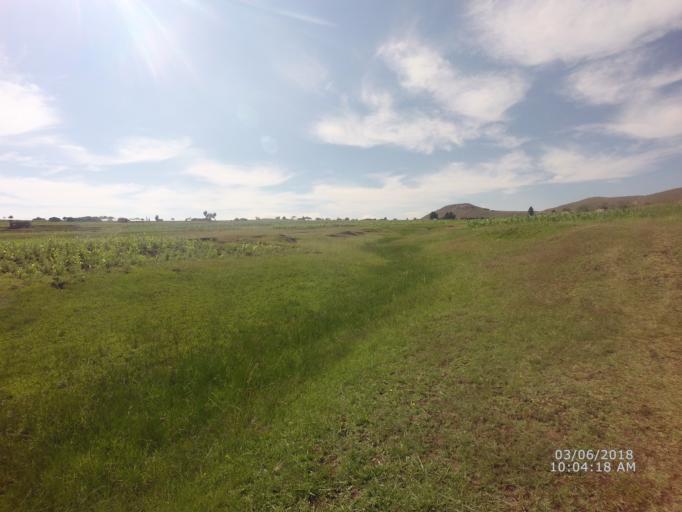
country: LS
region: Berea
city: Teyateyaneng
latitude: -29.2252
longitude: 27.8653
